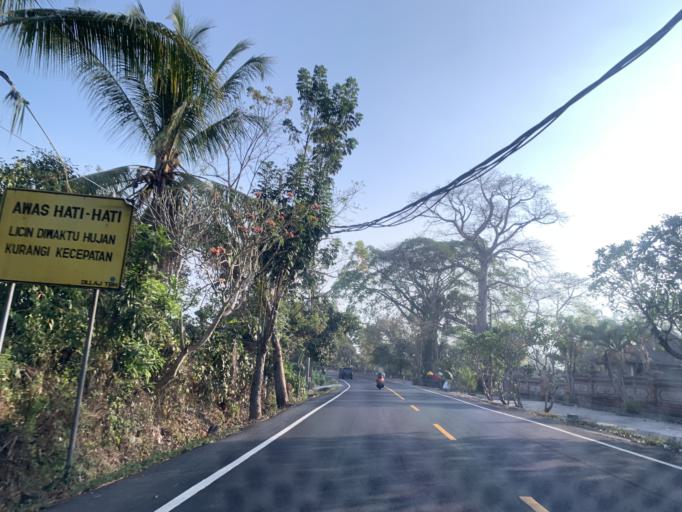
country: ID
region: Bali
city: Banjar Delodrurung
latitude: -8.5003
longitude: 115.0184
